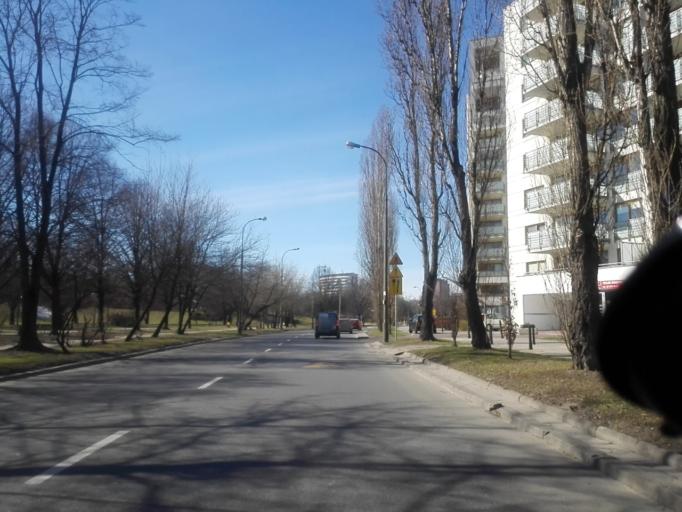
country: PL
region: Masovian Voivodeship
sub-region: Warszawa
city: Ochota
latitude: 52.2011
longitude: 20.9751
